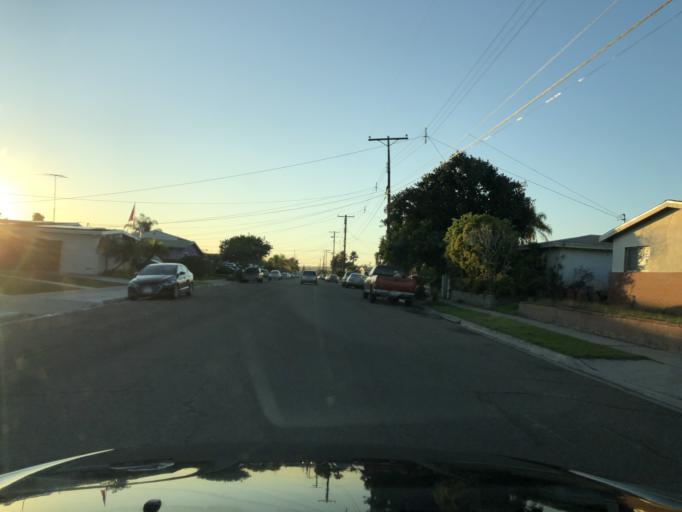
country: US
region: California
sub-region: San Diego County
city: La Jolla
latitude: 32.8294
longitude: -117.1762
